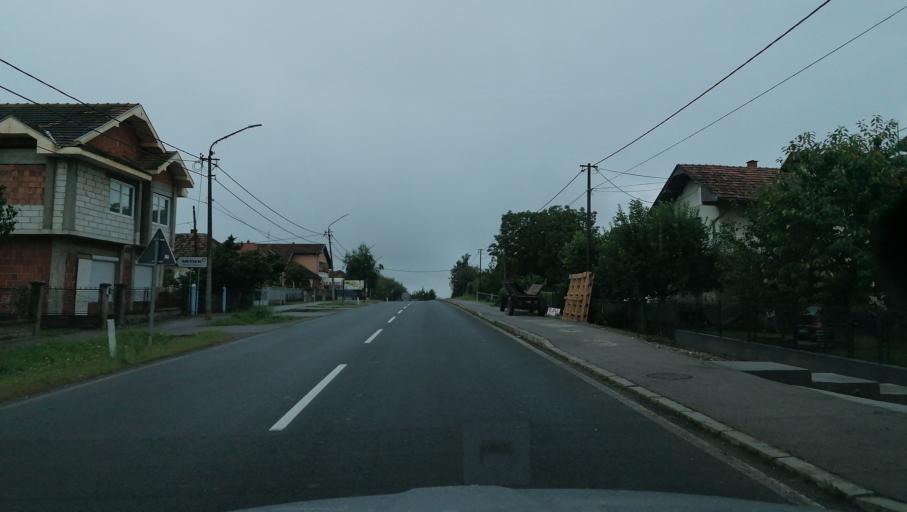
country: RS
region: Central Serbia
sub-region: Rasinski Okrug
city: Krusevac
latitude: 43.5879
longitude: 21.2678
